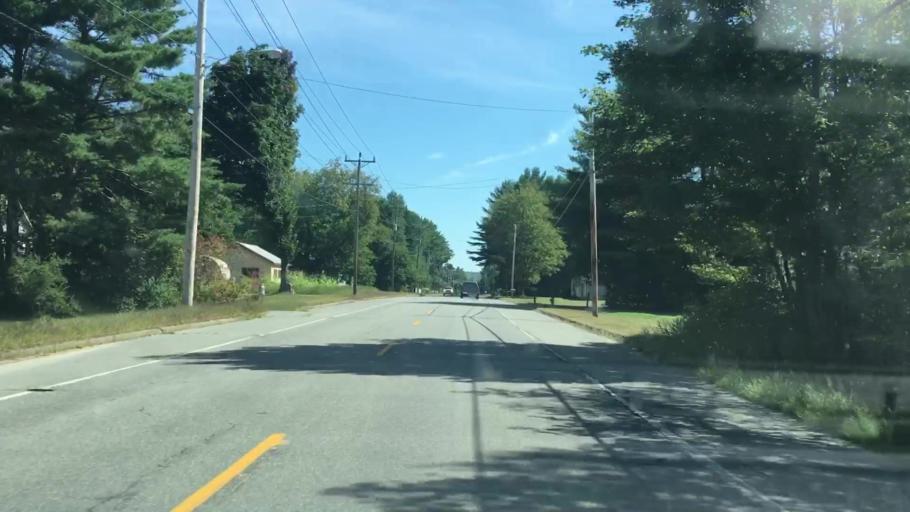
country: US
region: Maine
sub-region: Piscataquis County
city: Milo
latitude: 45.2408
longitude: -68.9699
